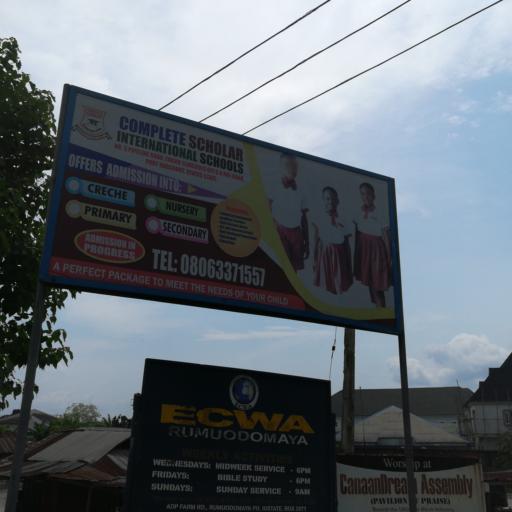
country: NG
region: Rivers
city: Port Harcourt
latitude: 4.8734
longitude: 7.0133
